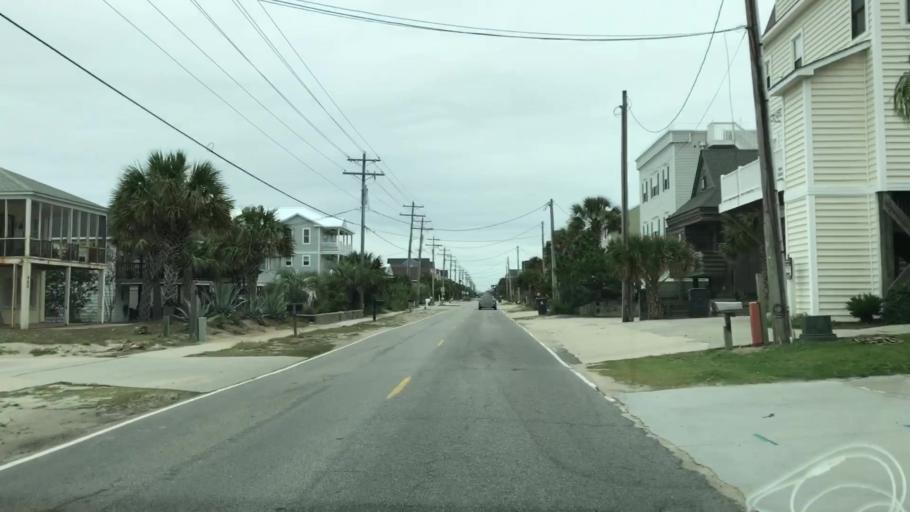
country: US
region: South Carolina
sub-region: Horry County
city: Garden City
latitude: 33.5700
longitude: -79.0047
